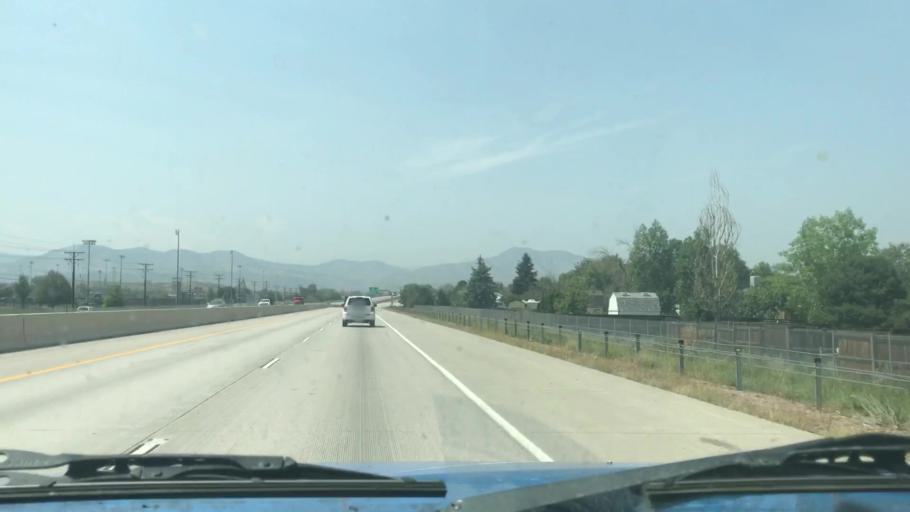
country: US
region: Colorado
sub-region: Jefferson County
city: Lakewood
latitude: 39.6517
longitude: -105.1045
